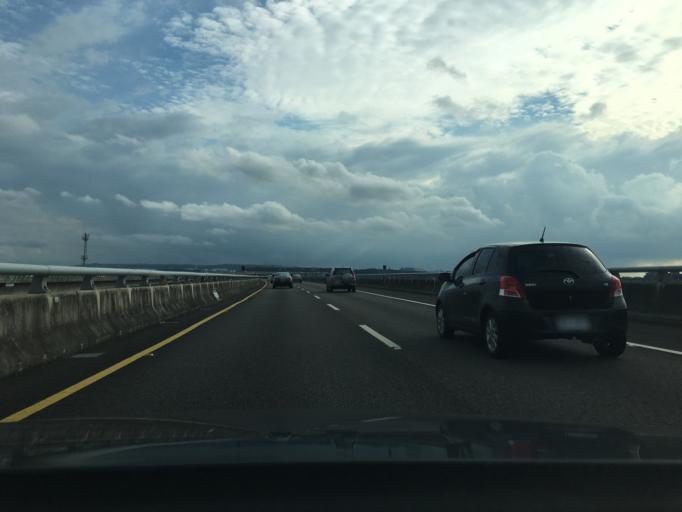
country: TW
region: Taiwan
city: Taoyuan City
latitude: 24.9524
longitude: 121.1965
